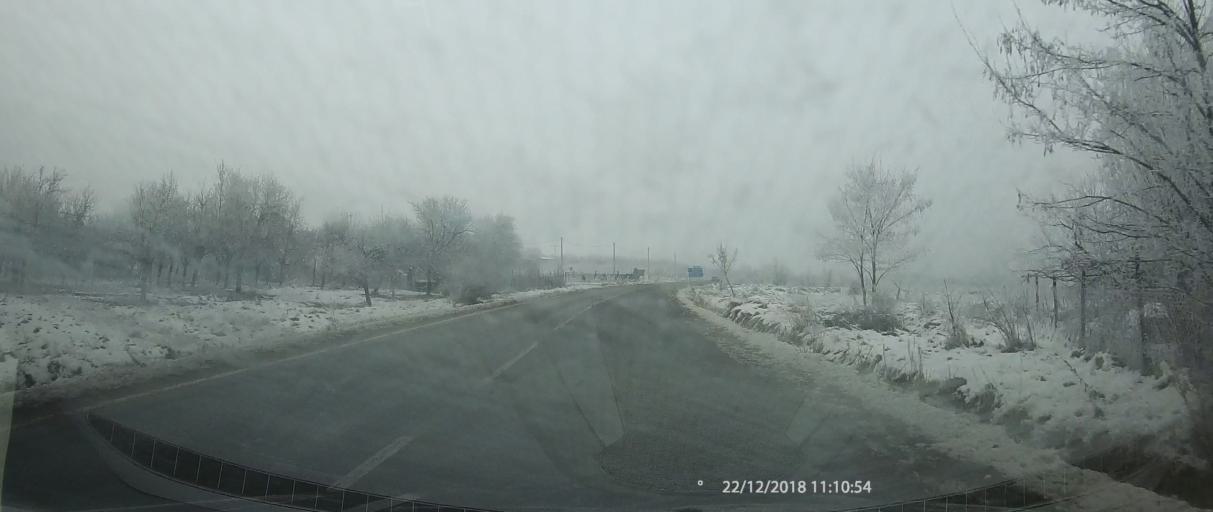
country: BG
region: Kyustendil
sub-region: Obshtina Kyustendil
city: Kyustendil
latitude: 42.2793
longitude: 22.6567
